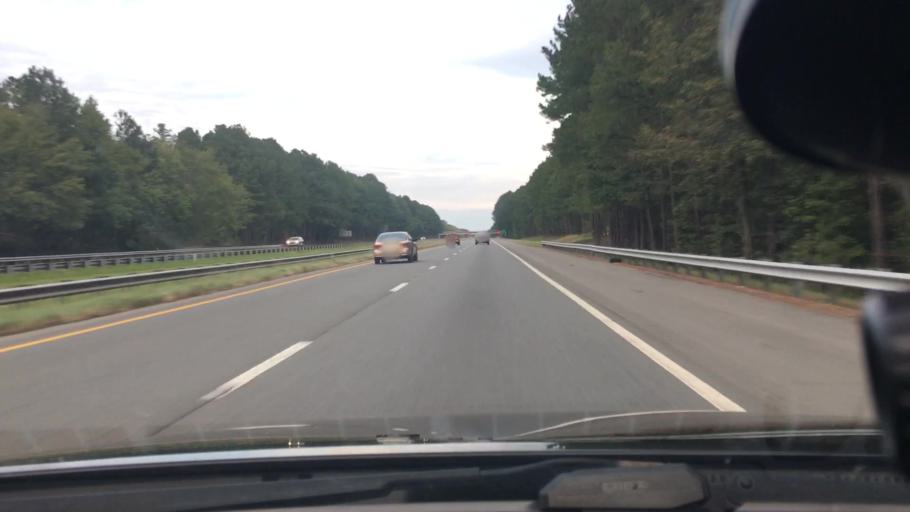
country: US
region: North Carolina
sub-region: Chatham County
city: Farmville
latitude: 35.5725
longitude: -79.1417
